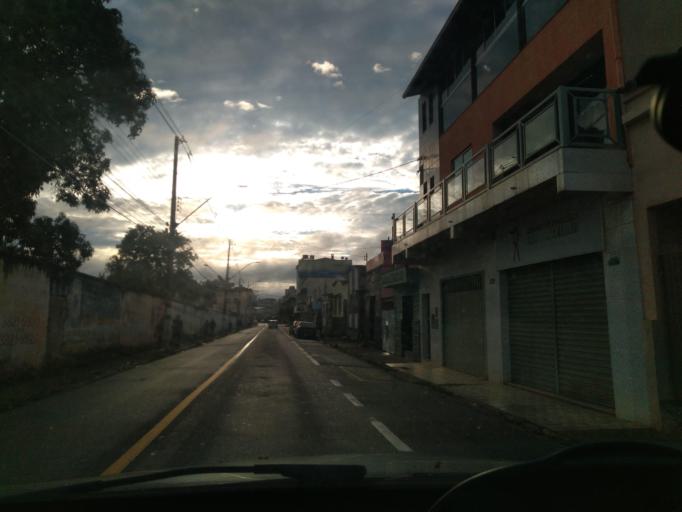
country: BR
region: Minas Gerais
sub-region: Lavras
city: Lavras
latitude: -21.2467
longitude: -45.0120
